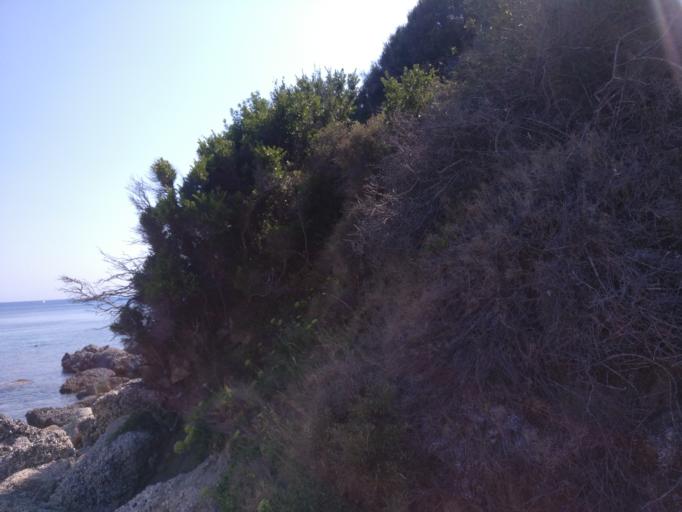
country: GR
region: Ionian Islands
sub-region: Nomos Kerkyras
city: Agios Georgis
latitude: 39.7219
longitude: 19.6641
